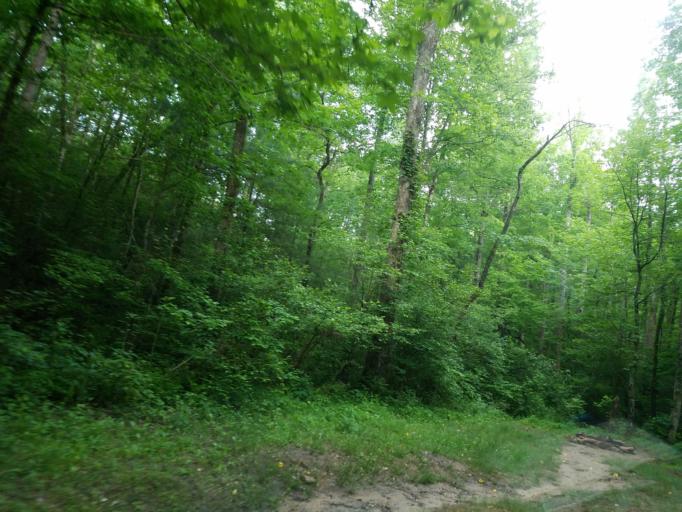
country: US
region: Georgia
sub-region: Lumpkin County
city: Dahlonega
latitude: 34.5930
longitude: -84.1185
